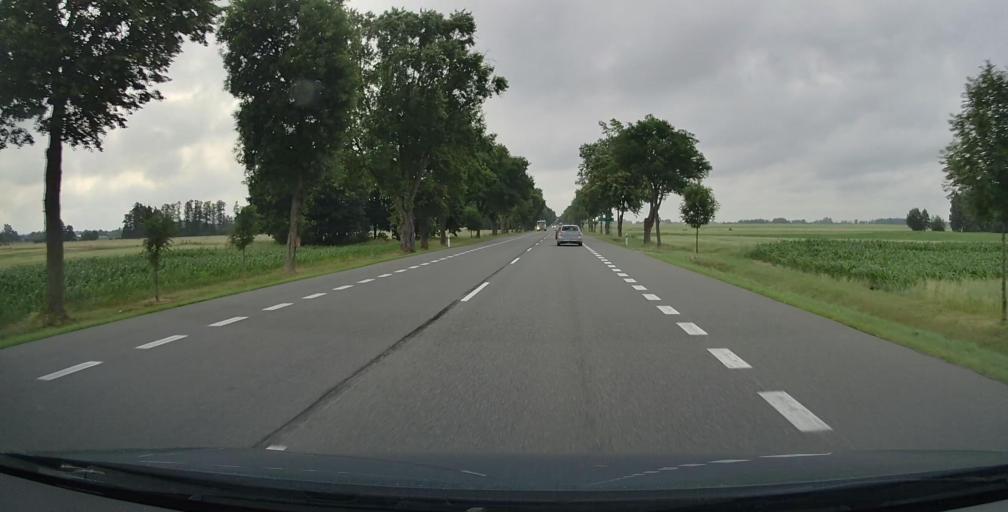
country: PL
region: Lublin Voivodeship
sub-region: Powiat lukowski
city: Trzebieszow
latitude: 52.0667
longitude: 22.5355
